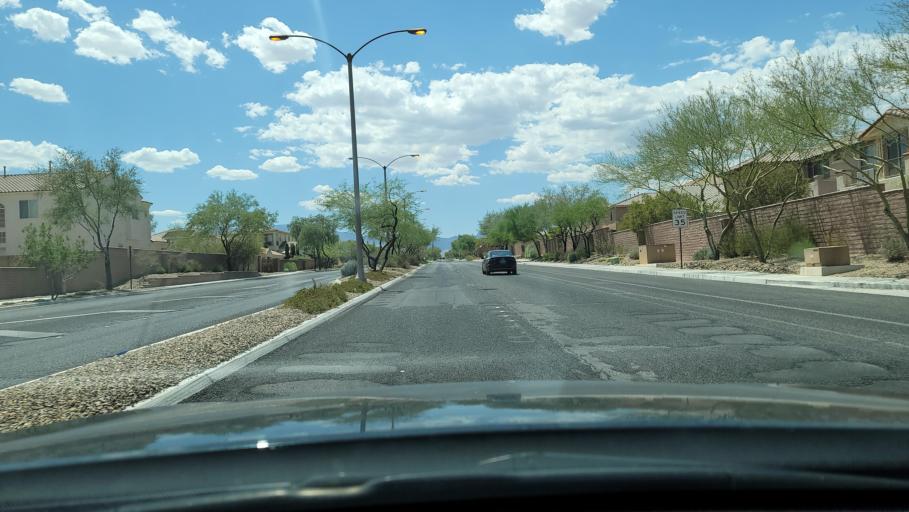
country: US
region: Nevada
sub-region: Clark County
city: Enterprise
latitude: 36.0123
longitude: -115.2625
